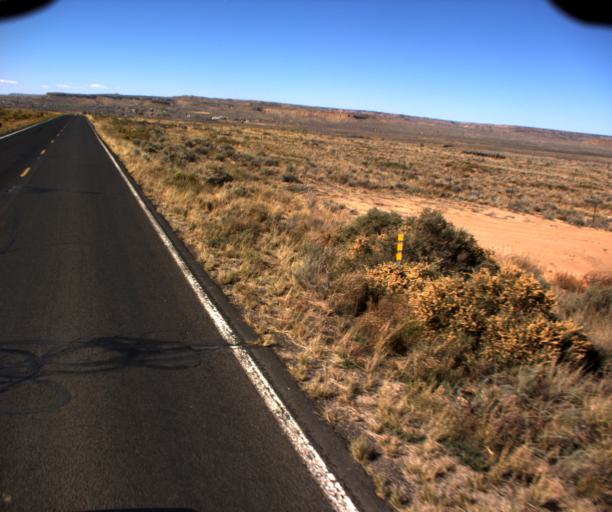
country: US
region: Arizona
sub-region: Navajo County
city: First Mesa
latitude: 35.8730
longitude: -110.5709
